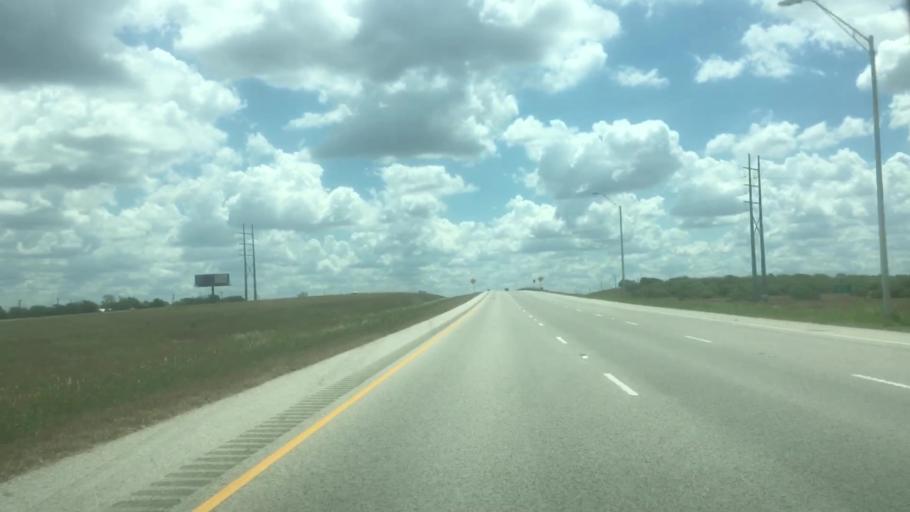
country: US
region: Texas
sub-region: Caldwell County
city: Uhland
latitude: 30.0100
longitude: -97.6879
